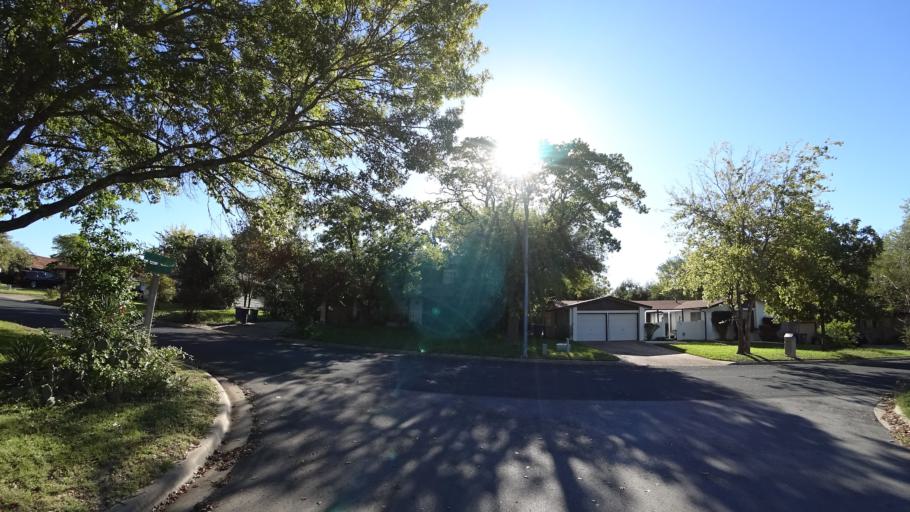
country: US
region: Texas
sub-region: Travis County
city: Austin
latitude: 30.3073
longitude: -97.6632
